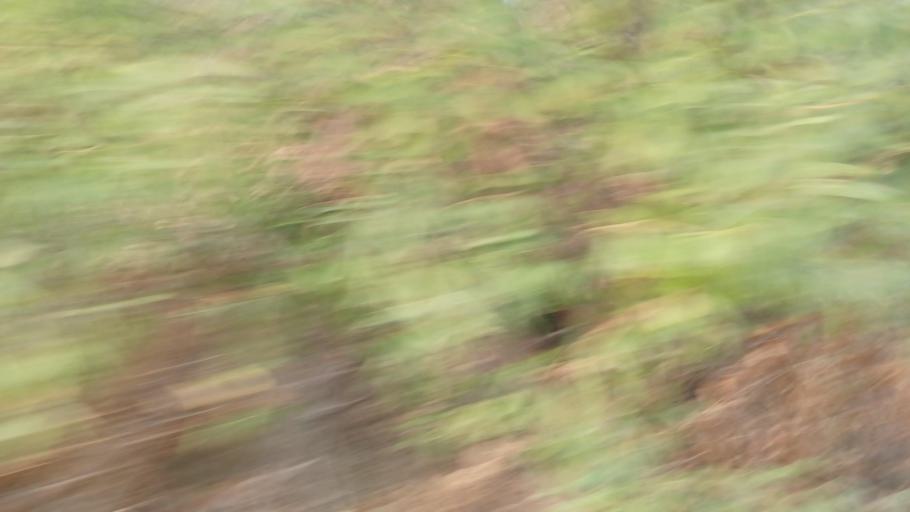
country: CY
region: Pafos
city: Mesogi
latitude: 34.8462
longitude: 32.5344
